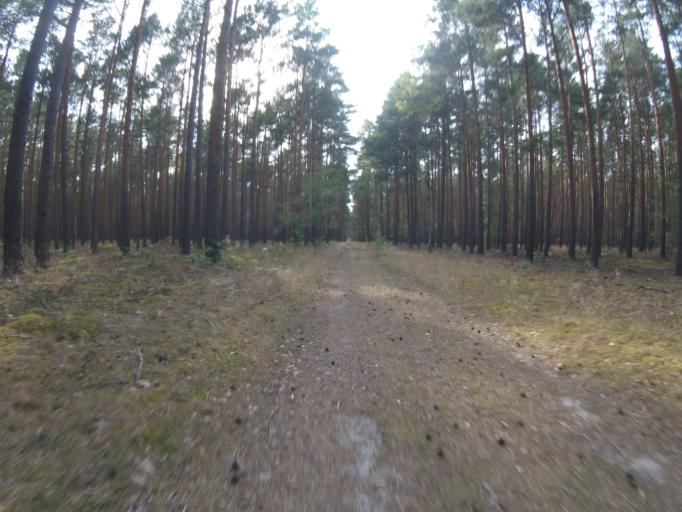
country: DE
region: Brandenburg
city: Gross Koris
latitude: 52.2096
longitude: 13.7401
